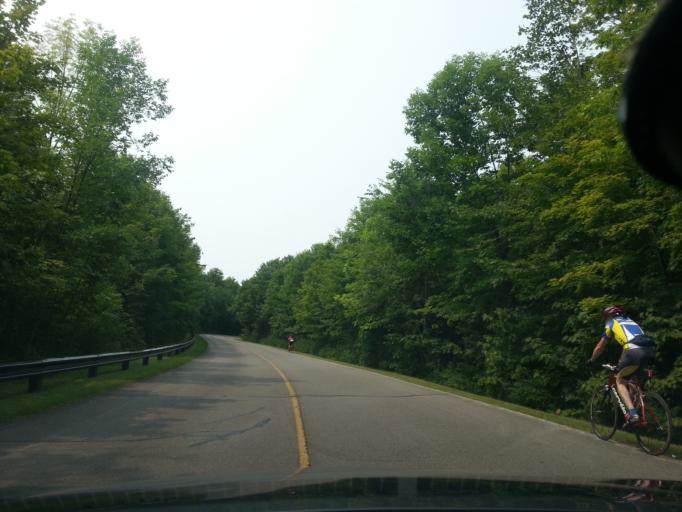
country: CA
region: Quebec
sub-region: Outaouais
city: Gatineau
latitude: 45.4670
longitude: -75.7988
